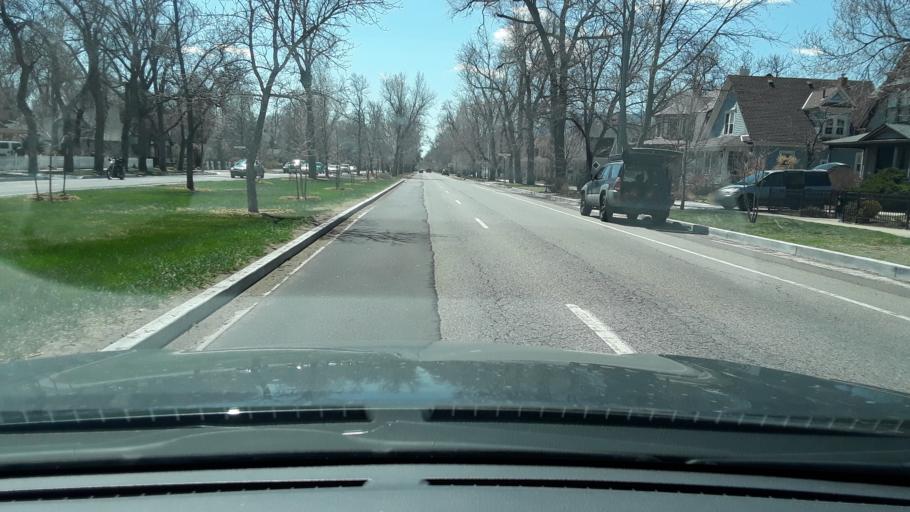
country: US
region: Colorado
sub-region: El Paso County
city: Colorado Springs
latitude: 38.8639
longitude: -104.8202
